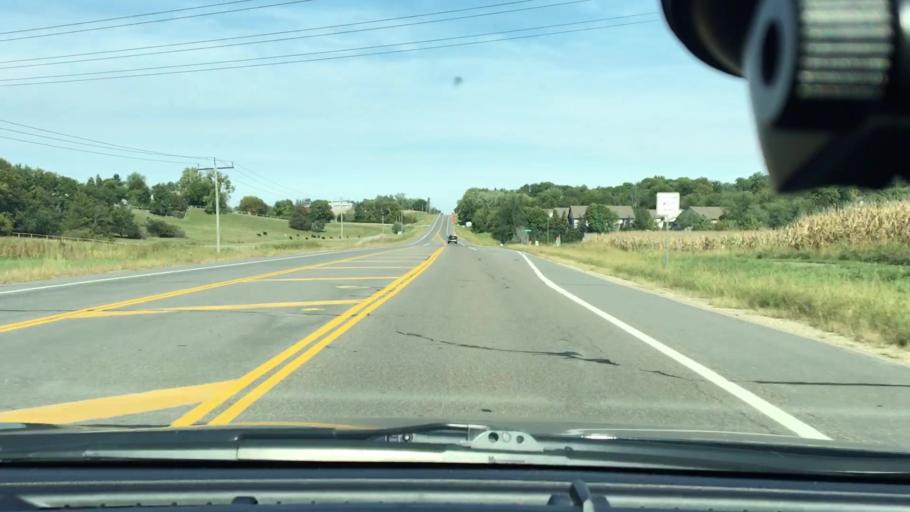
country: US
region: Minnesota
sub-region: Wright County
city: Hanover
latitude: 45.1764
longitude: -93.6656
